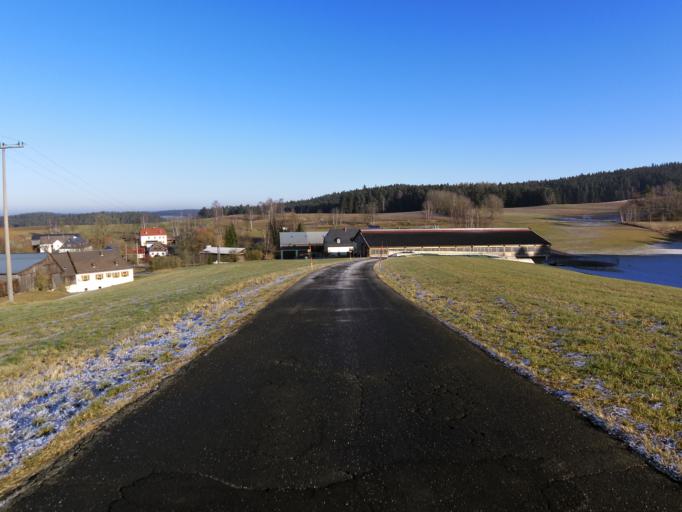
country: DE
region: Bavaria
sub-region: Upper Franconia
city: Roslau
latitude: 50.0839
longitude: 12.0284
